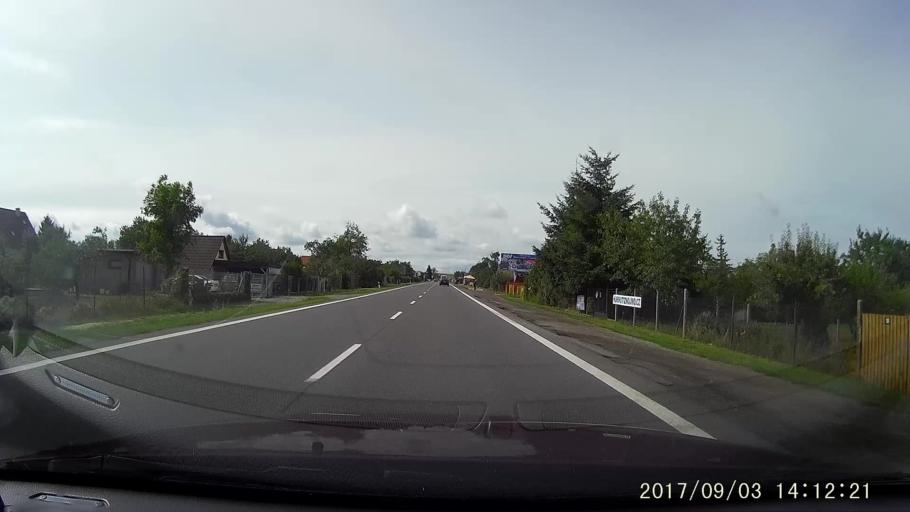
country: CZ
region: South Moravian
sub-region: Okres Znojmo
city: Znojmo
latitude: 48.8707
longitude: 16.0288
